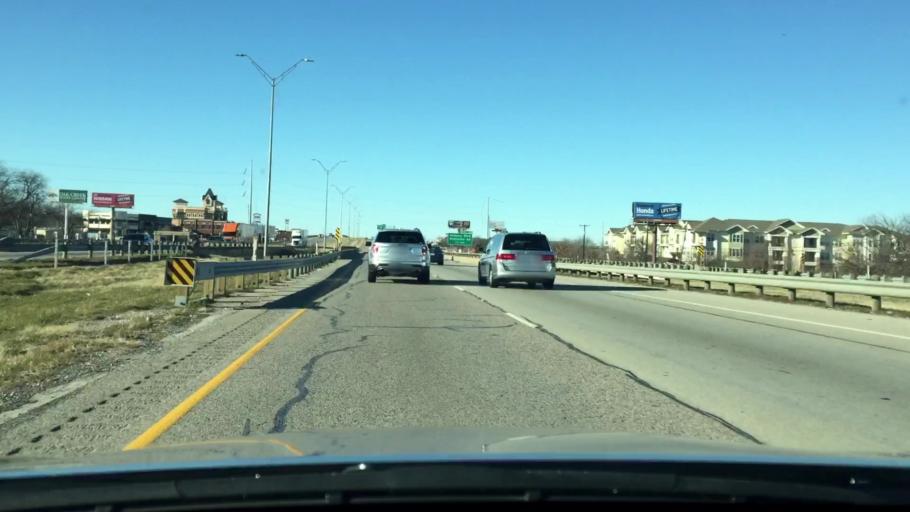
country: US
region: Texas
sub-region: Johnson County
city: Burleson
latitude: 32.5396
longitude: -97.3128
